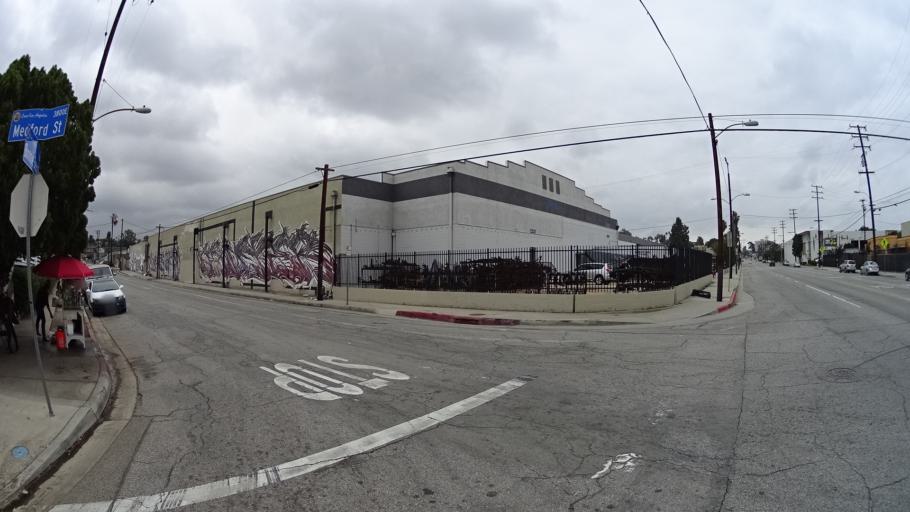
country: US
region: California
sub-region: Los Angeles County
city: Belvedere
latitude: 34.0600
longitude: -118.1836
